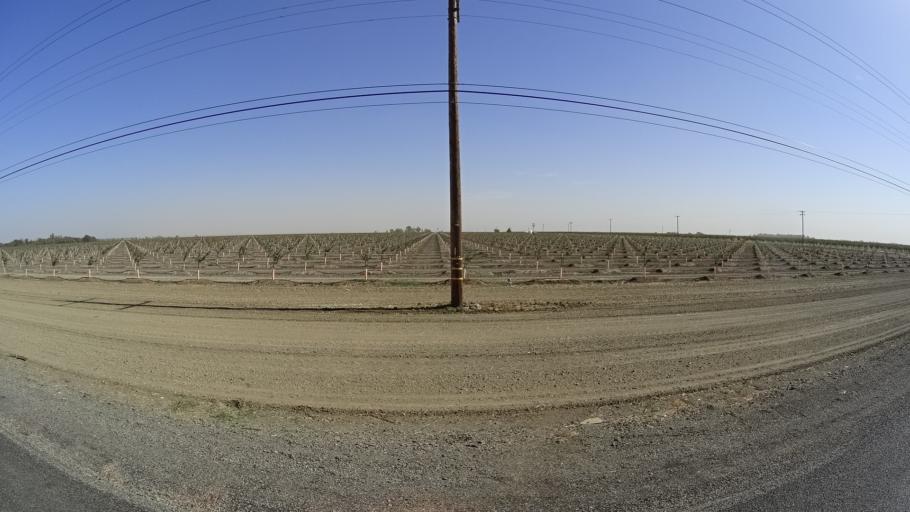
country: US
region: California
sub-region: Yolo County
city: Woodland
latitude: 38.6195
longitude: -121.7297
